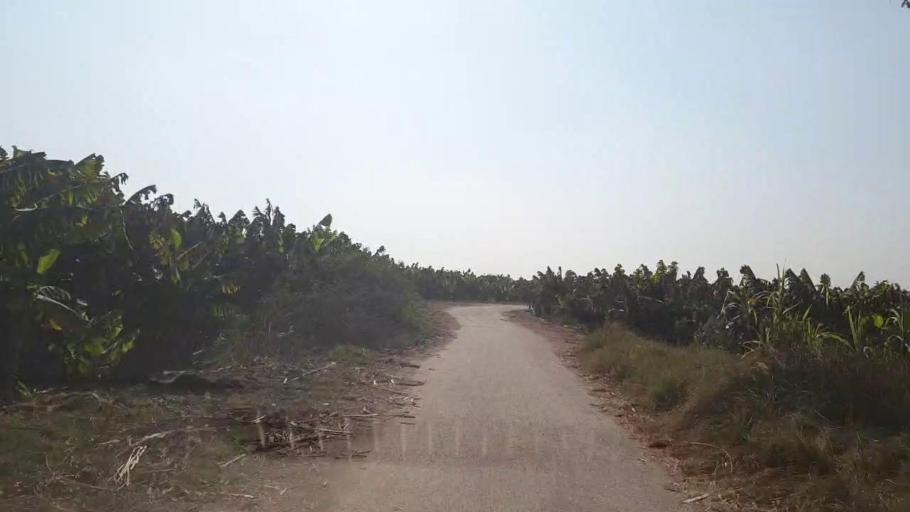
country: PK
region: Sindh
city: Tando Allahyar
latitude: 25.5936
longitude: 68.7535
